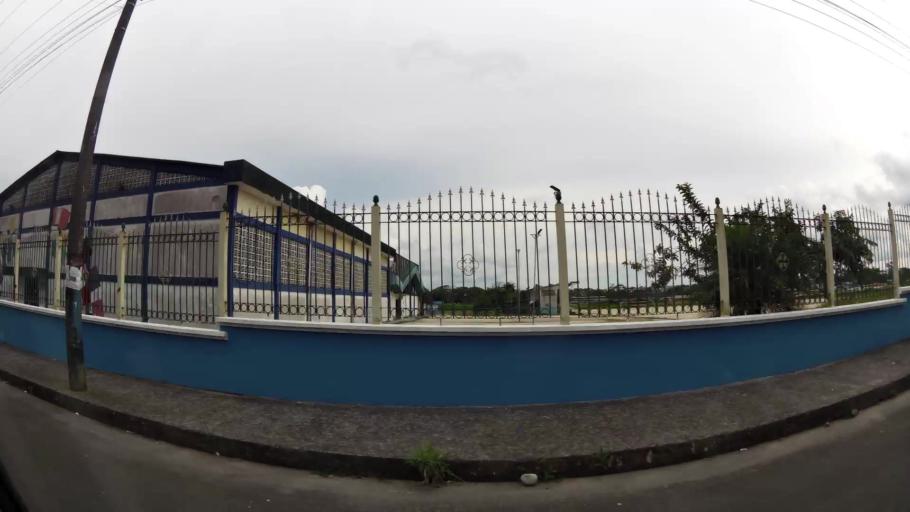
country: EC
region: Pastaza
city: Puyo
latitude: -1.4941
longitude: -78.0105
